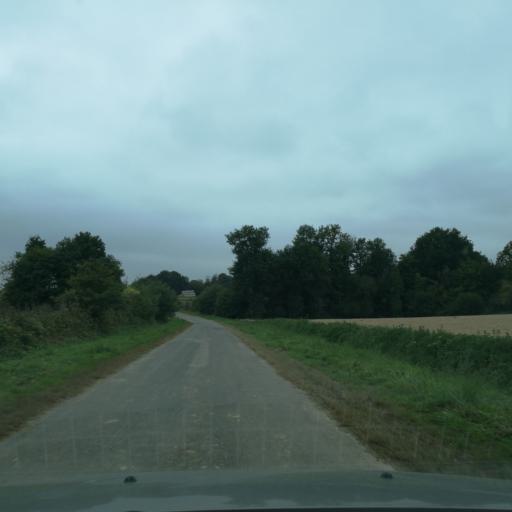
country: FR
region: Brittany
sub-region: Departement d'Ille-et-Vilaine
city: Montauban-de-Bretagne
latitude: 48.1859
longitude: -2.0195
